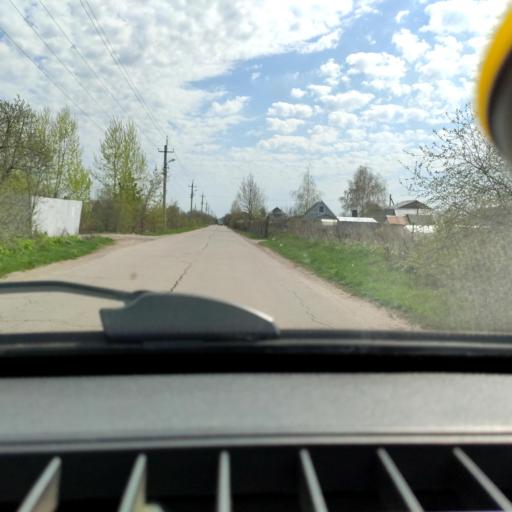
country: RU
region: Samara
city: Tol'yatti
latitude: 53.7006
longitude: 49.4349
